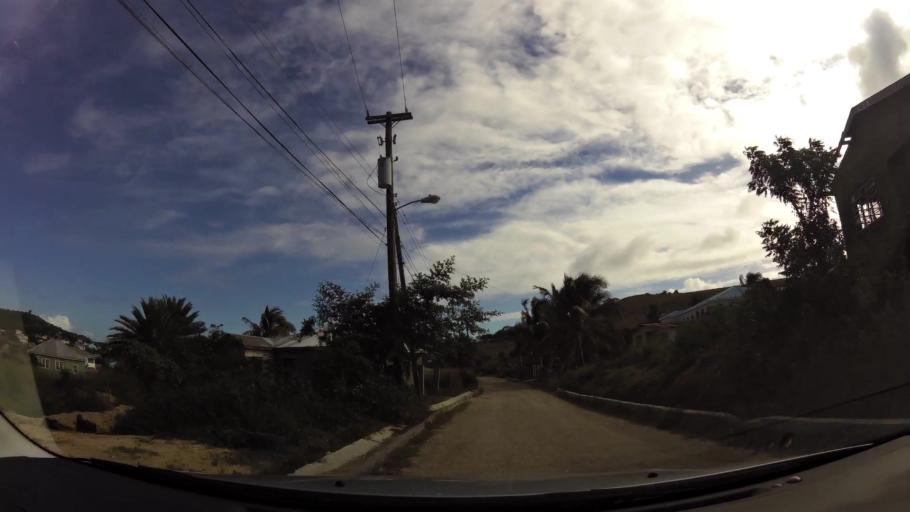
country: AG
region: Saint Peter
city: All Saints
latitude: 17.0486
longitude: -61.8005
